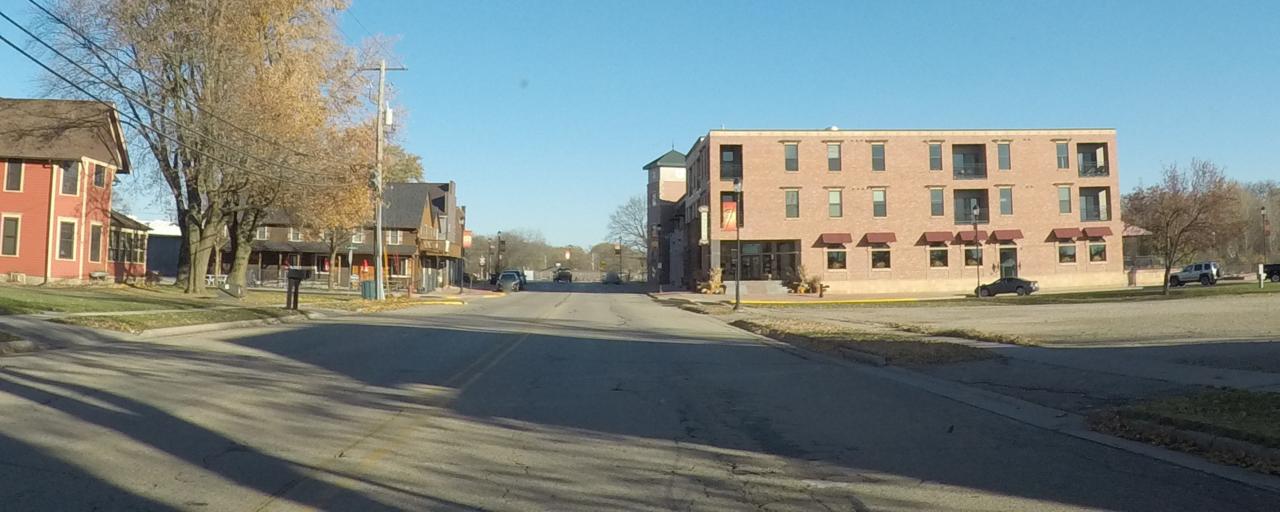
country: US
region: Wisconsin
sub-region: Dane County
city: Cottage Grove
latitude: 43.0748
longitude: -89.1997
